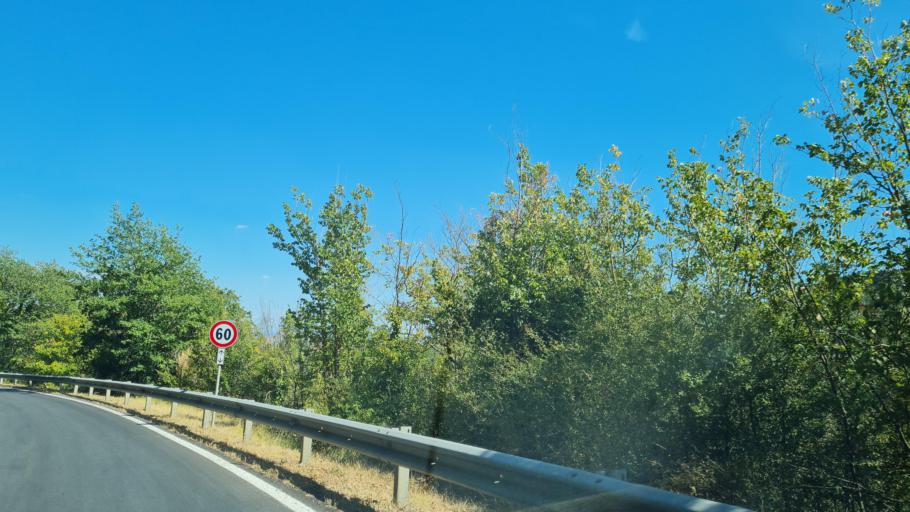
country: IT
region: Tuscany
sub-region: Provincia di Siena
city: Sant'Albino
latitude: 43.0747
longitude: 11.7973
